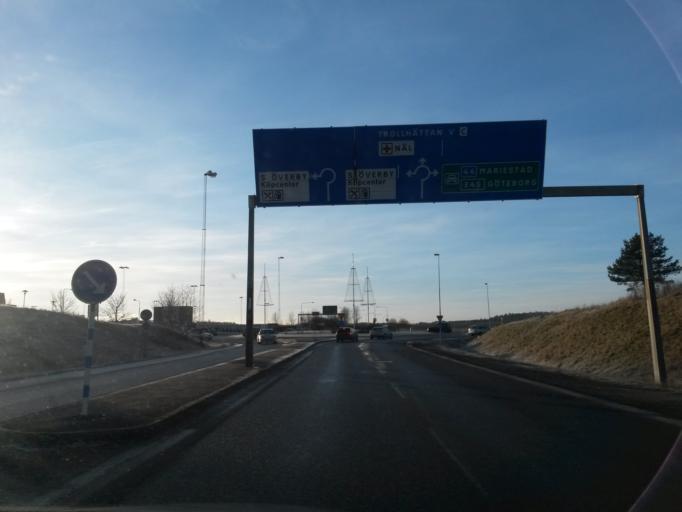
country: SE
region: Vaestra Goetaland
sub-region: Trollhattan
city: Trollhattan
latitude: 58.3163
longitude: 12.3062
